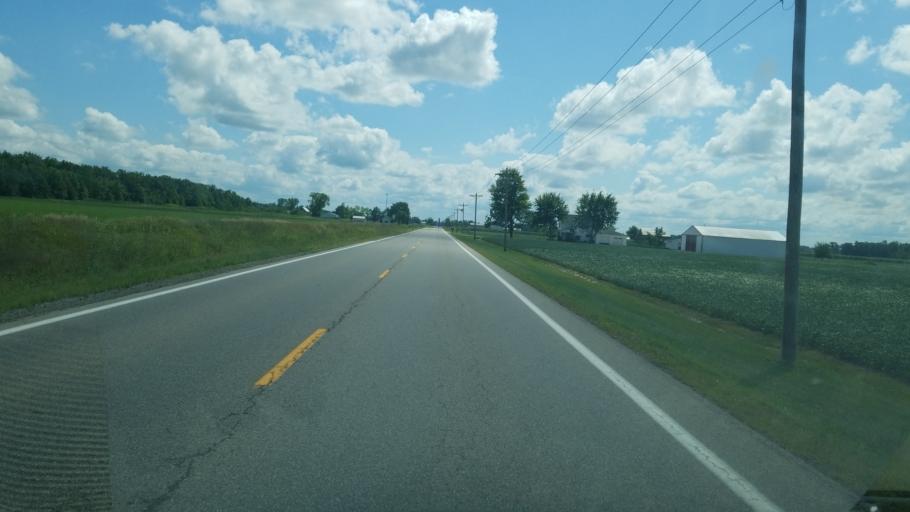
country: US
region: Ohio
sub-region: Putnam County
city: Kalida
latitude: 41.0204
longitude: -84.1980
